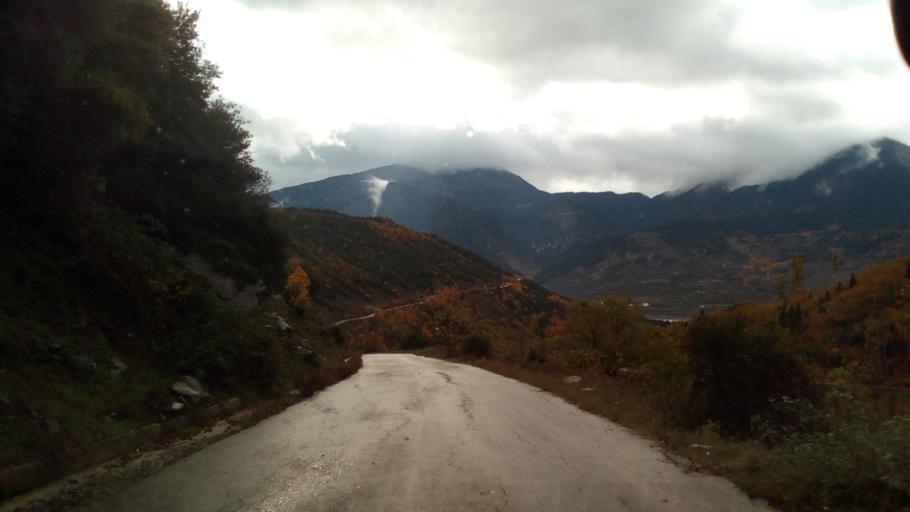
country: GR
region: West Greece
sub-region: Nomos Aitolias kai Akarnanias
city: Thermo
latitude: 38.6847
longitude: 21.8426
